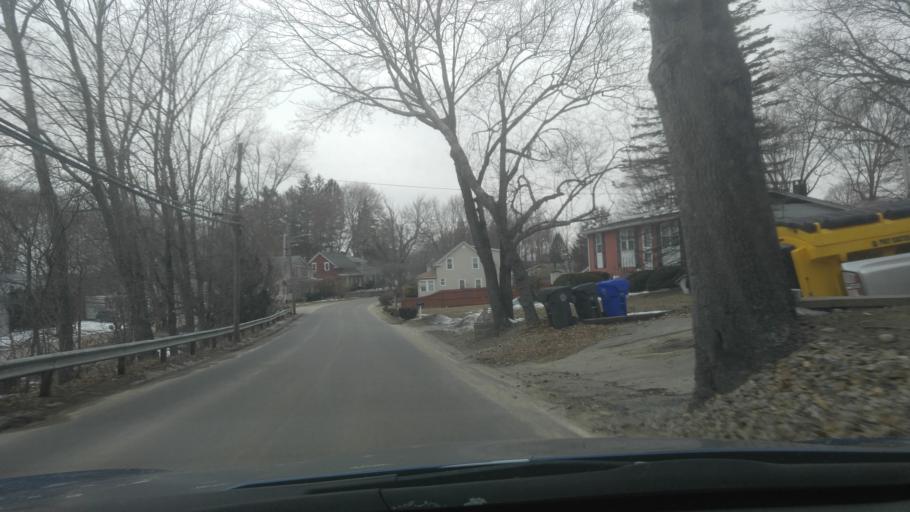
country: US
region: Rhode Island
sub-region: Kent County
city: West Warwick
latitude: 41.6793
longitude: -71.5222
